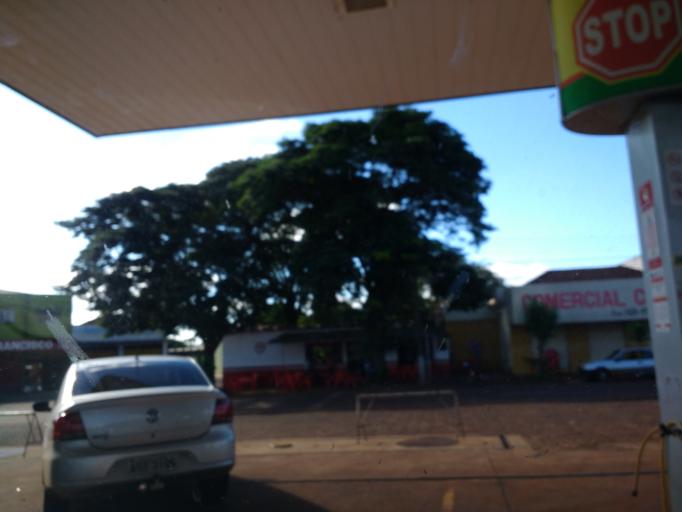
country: BR
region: Parana
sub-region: Palotina
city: Palotina
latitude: -24.4110
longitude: -53.5227
